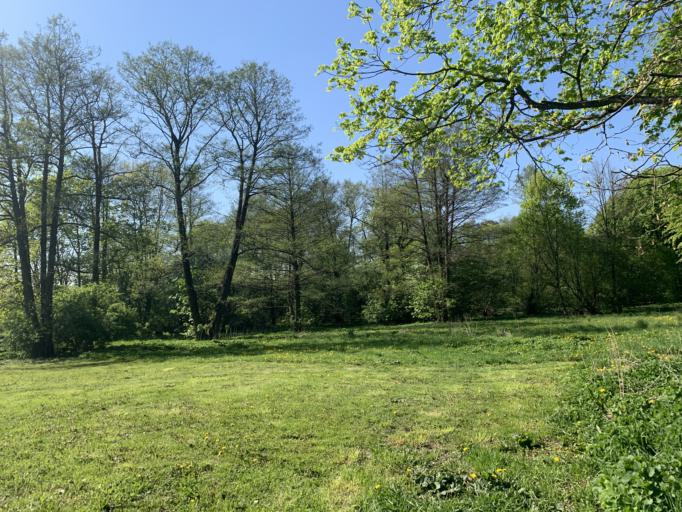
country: BY
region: Minsk
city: Kapyl'
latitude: 53.2594
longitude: 26.9492
